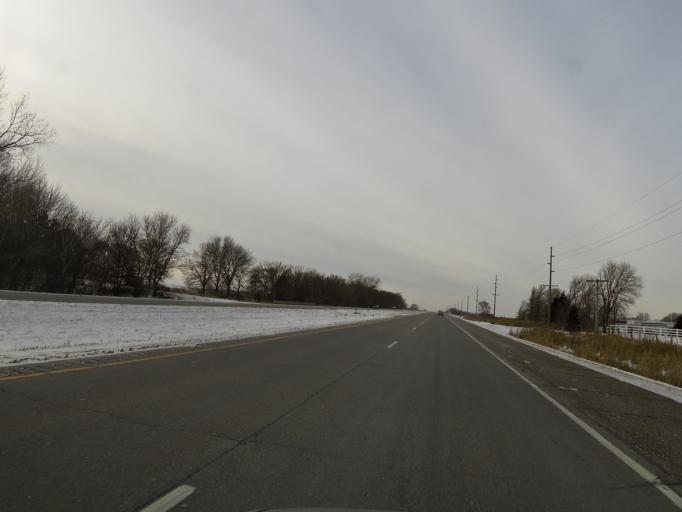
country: US
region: Minnesota
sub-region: Scott County
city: Belle Plaine
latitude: 44.6407
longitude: -93.7162
